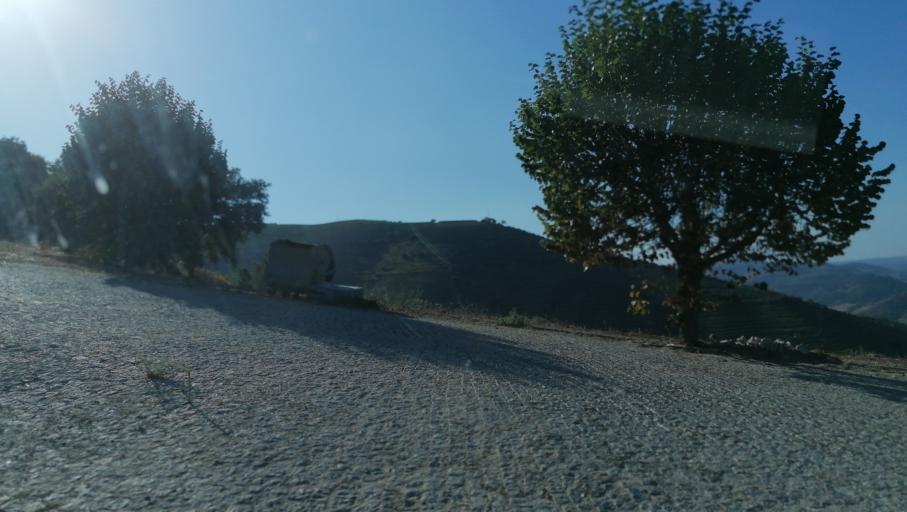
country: PT
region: Viseu
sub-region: Sao Joao da Pesqueira
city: Sao Joao da Pesqueira
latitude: 41.1867
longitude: -7.4105
